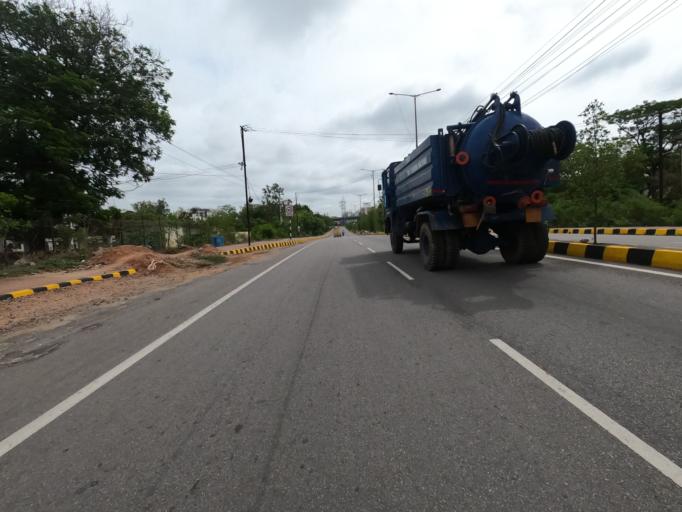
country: IN
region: Telangana
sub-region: Hyderabad
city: Hyderabad
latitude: 17.3423
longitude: 78.4142
